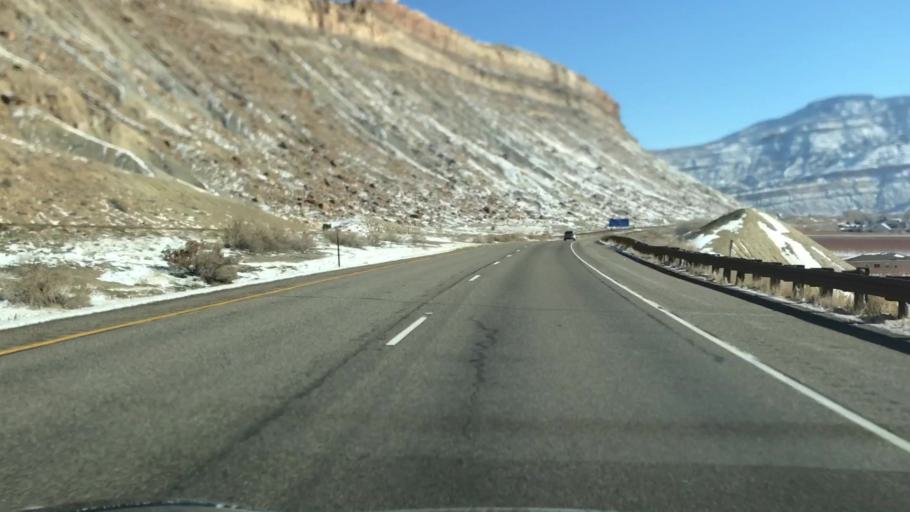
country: US
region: Colorado
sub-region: Mesa County
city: Palisade
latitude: 39.1204
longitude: -108.3738
